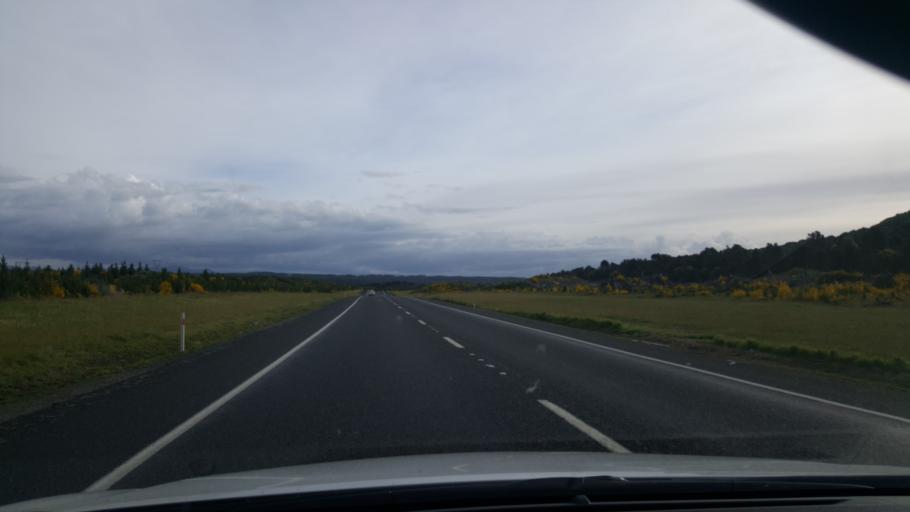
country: NZ
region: Waikato
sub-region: Taupo District
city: Taupo
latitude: -38.8468
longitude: 176.0576
